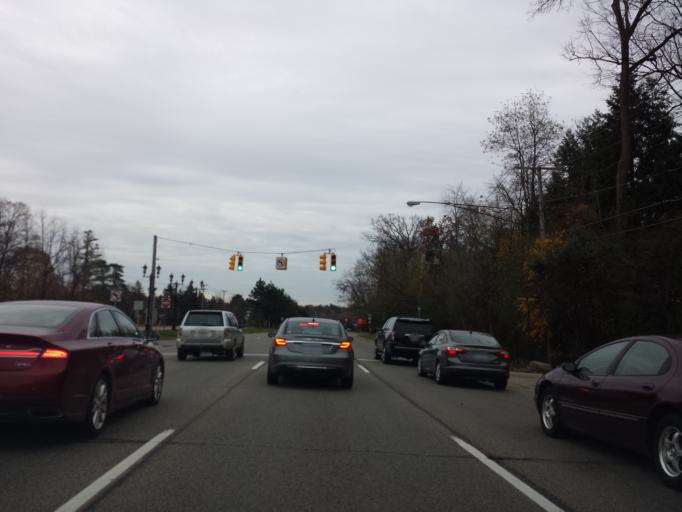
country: US
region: Michigan
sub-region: Oakland County
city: Bloomfield Hills
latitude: 42.5878
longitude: -83.2486
